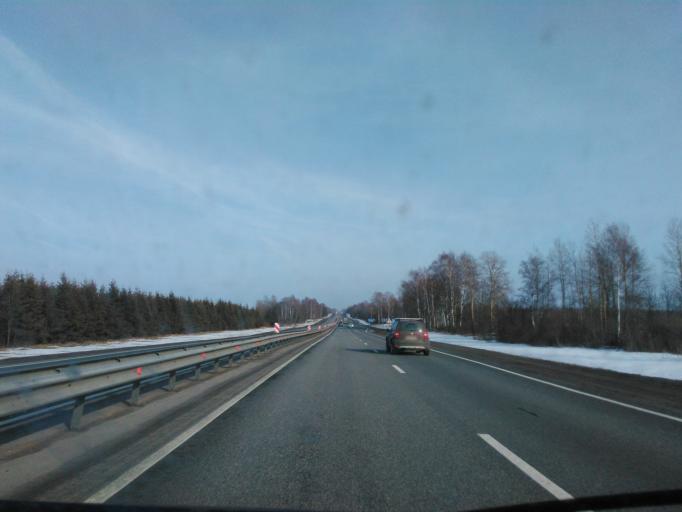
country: RU
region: Smolensk
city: Verkhnedneprovskiy
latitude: 55.1827
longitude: 33.6851
